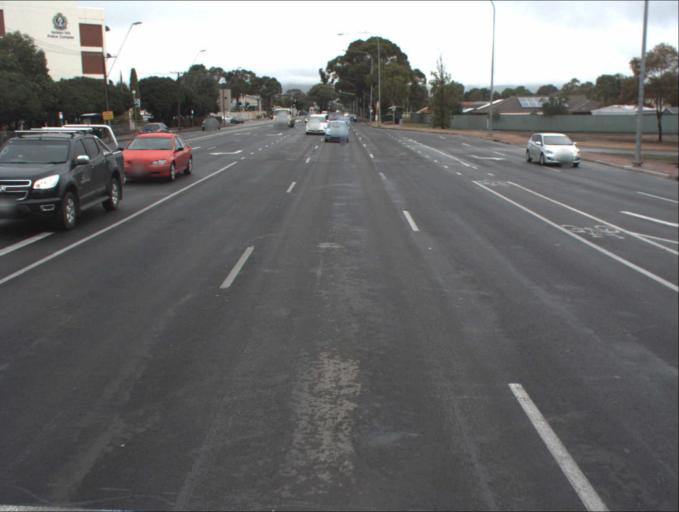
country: AU
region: South Australia
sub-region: Port Adelaide Enfield
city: Gilles Plains
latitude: -34.8573
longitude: 138.6556
